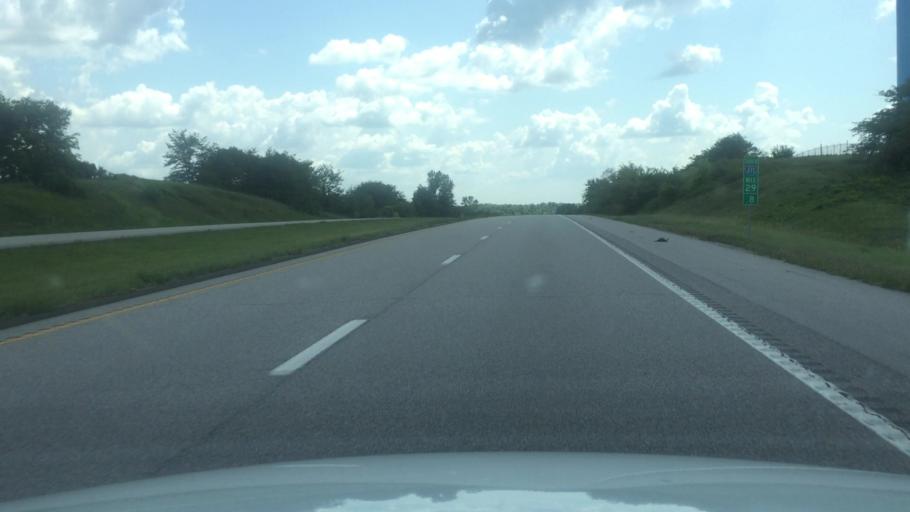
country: US
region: Missouri
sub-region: Platte County
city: Platte City
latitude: 39.3219
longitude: -94.7560
